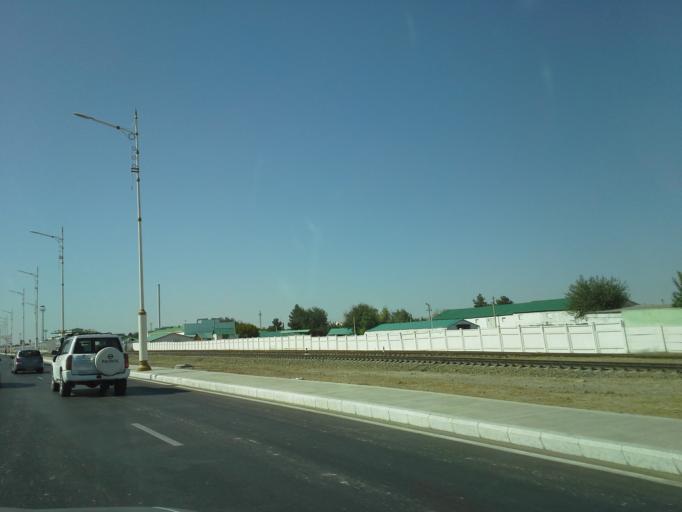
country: TM
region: Ahal
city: Ashgabat
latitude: 37.9318
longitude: 58.4172
